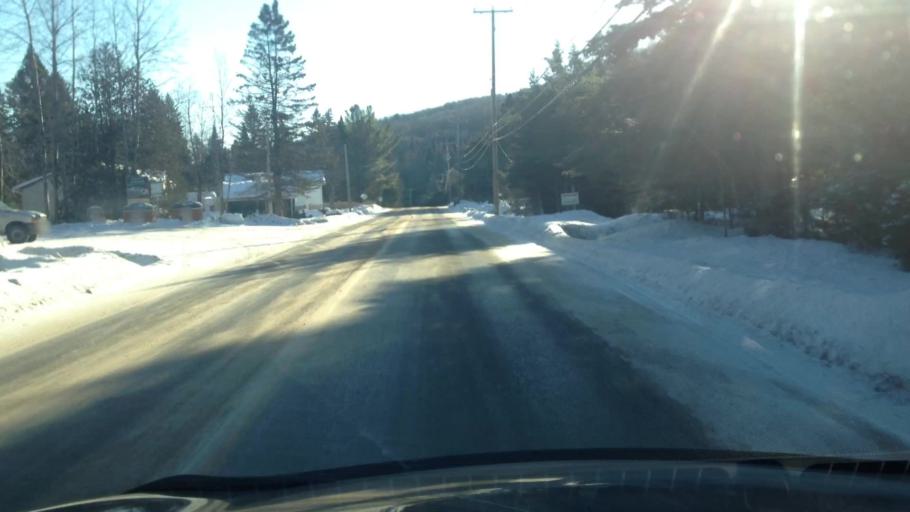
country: CA
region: Quebec
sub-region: Laurentides
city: Sainte-Agathe-des-Monts
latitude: 45.9226
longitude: -74.3908
